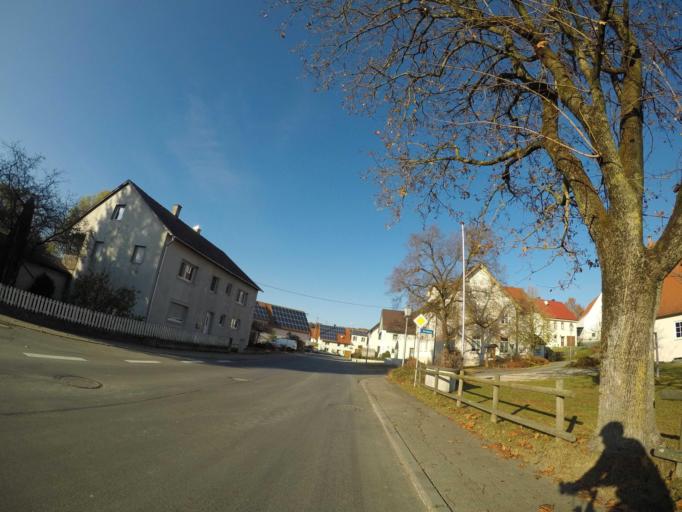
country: DE
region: Baden-Wuerttemberg
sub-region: Tuebingen Region
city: Grundsheim
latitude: 48.1777
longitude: 9.6677
